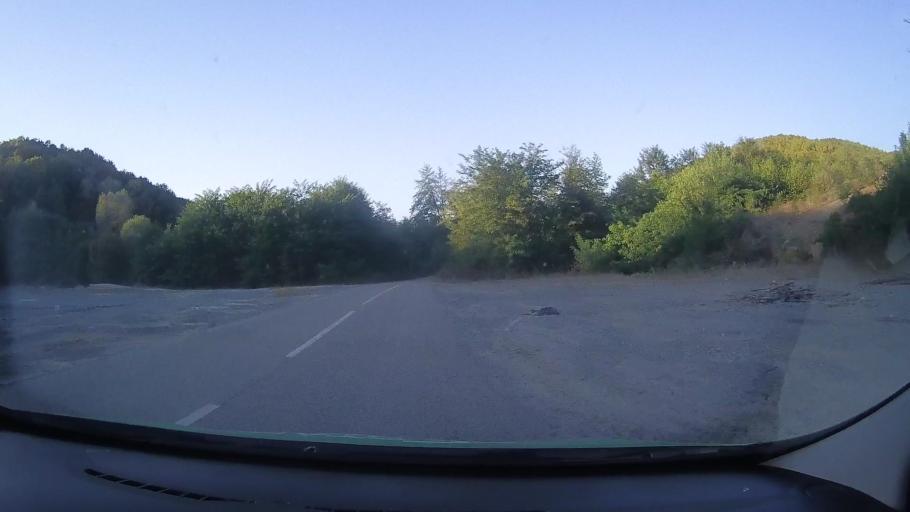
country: RO
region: Timis
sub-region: Comuna Fardea
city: Fardea
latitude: 45.6948
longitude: 22.1600
